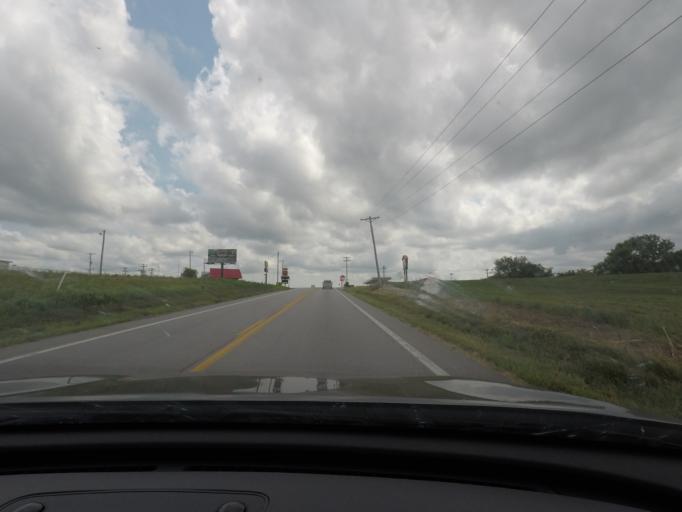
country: US
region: Missouri
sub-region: Lafayette County
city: Higginsville
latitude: 39.0055
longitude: -93.7353
